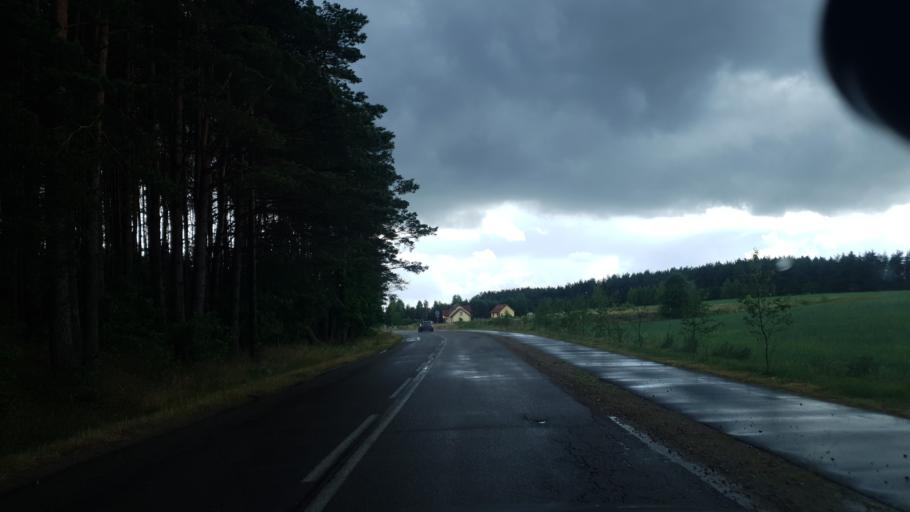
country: PL
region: Pomeranian Voivodeship
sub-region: Powiat kartuski
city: Stezyca
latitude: 54.2172
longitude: 17.9623
